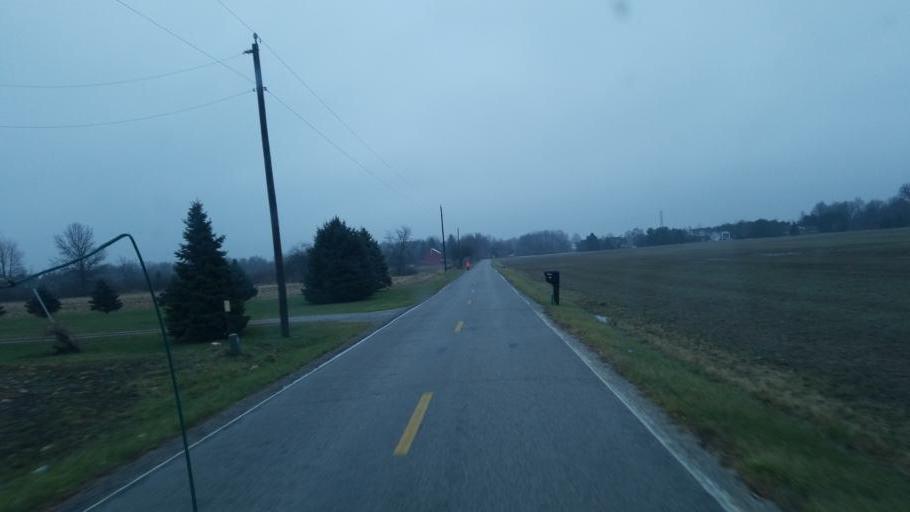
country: US
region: Ohio
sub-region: Delaware County
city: Delaware
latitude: 40.2732
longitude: -83.0003
